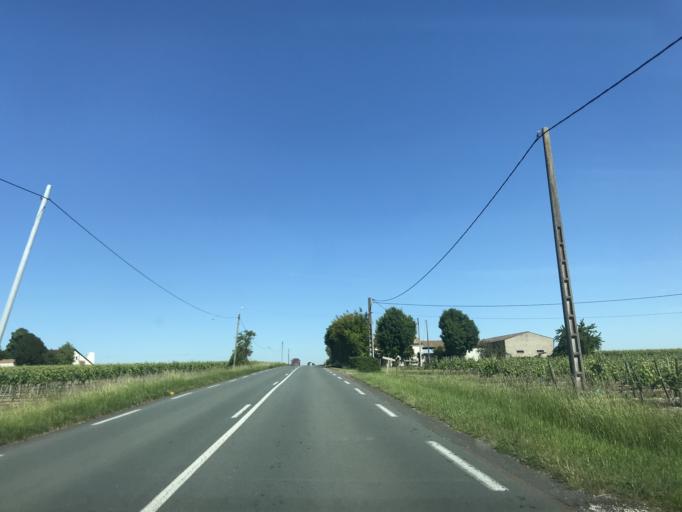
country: FR
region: Poitou-Charentes
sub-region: Departement de la Charente
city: Barbezieux-Saint-Hilaire
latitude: 45.5030
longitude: -0.2557
